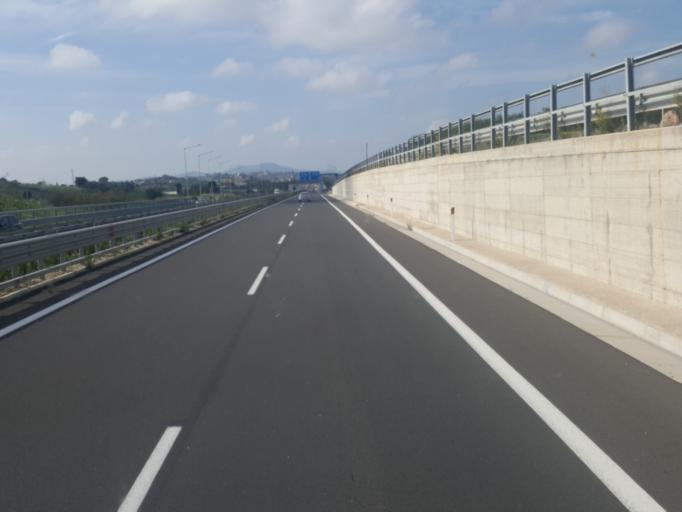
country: IT
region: Sicily
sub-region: Agrigento
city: Racalmuto
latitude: 37.3881
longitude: 13.7428
